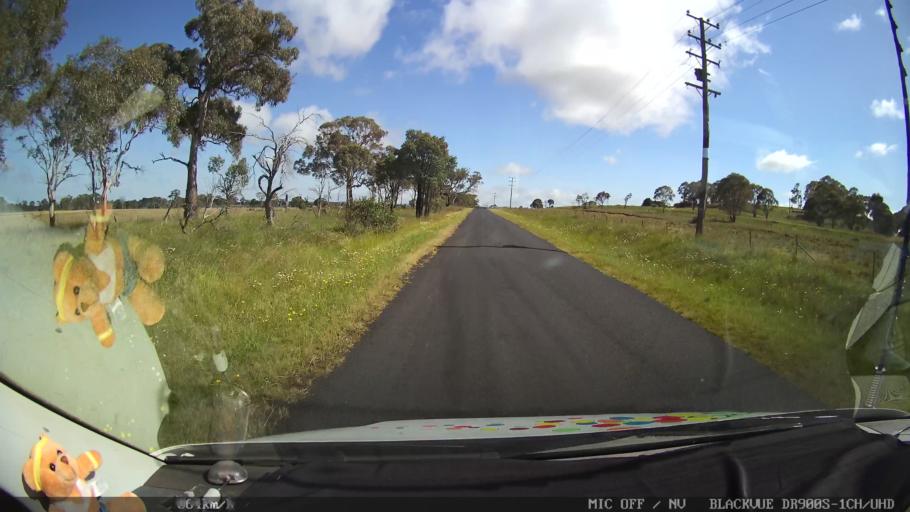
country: AU
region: New South Wales
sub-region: Guyra
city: Guyra
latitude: -30.1981
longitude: 151.6755
